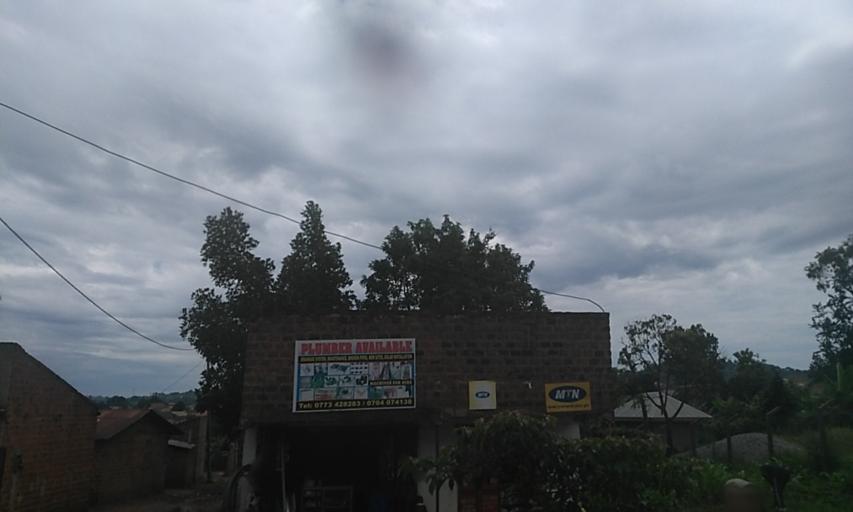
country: UG
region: Central Region
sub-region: Wakiso District
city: Bweyogerere
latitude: 0.3963
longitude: 32.6810
